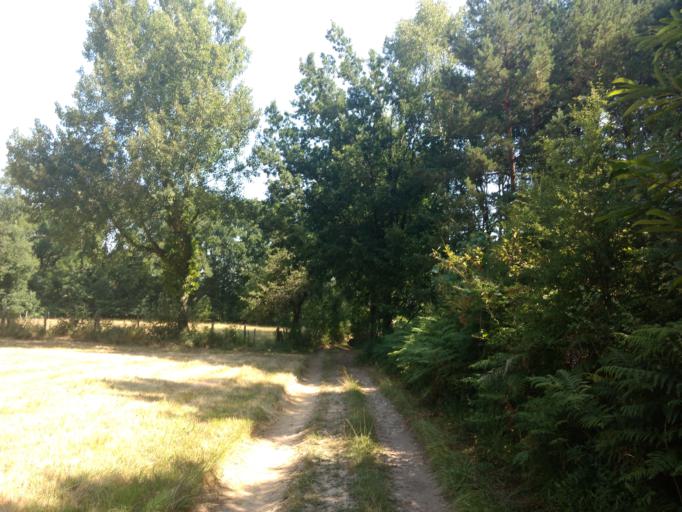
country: FR
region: Midi-Pyrenees
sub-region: Departement de l'Aveyron
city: Livinhac-le-Haut
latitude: 44.6058
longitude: 2.1589
